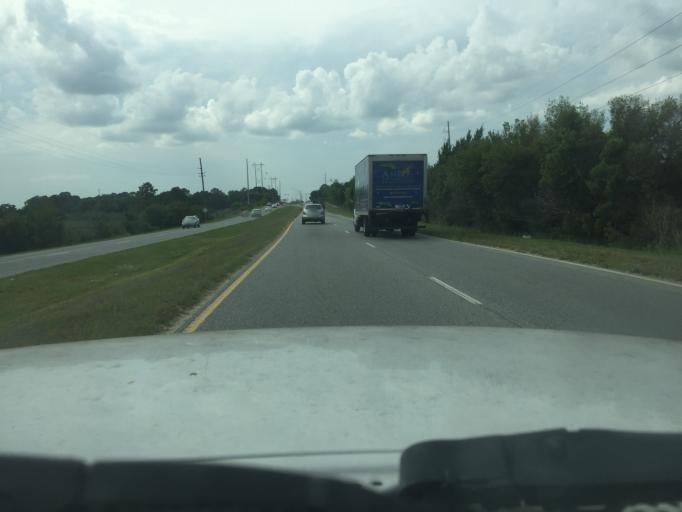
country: US
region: Georgia
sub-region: Chatham County
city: Whitemarsh Island
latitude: 32.0595
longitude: -81.0242
